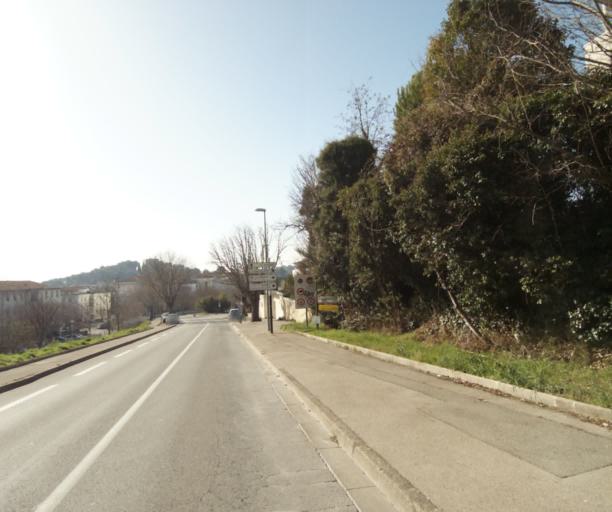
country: FR
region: Provence-Alpes-Cote d'Azur
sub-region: Departement des Bouches-du-Rhone
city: Aix-en-Provence
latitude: 43.5437
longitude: 5.4553
